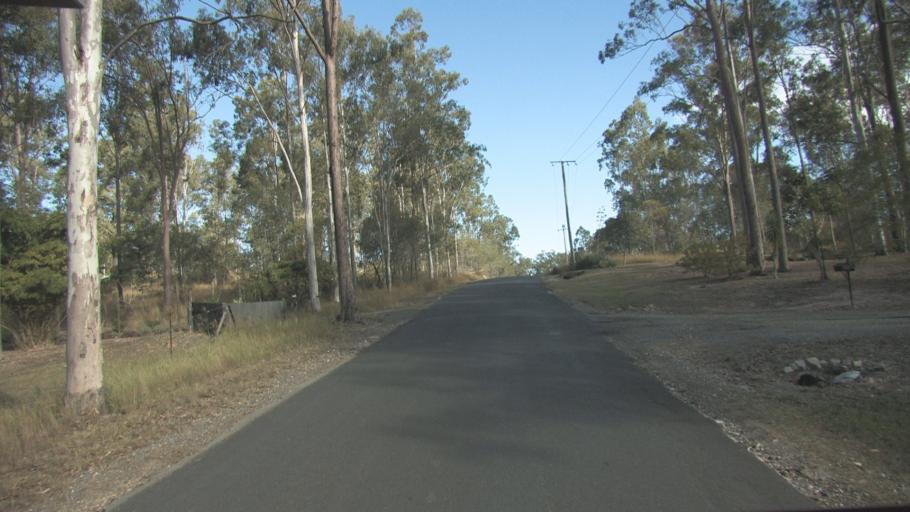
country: AU
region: Queensland
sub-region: Logan
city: Cedar Vale
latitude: -27.8326
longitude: 153.0611
